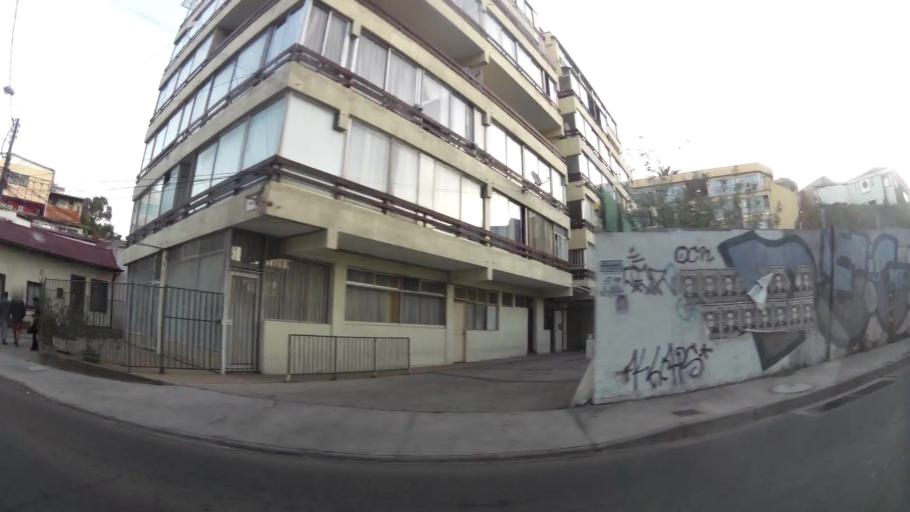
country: CL
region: Valparaiso
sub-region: Provincia de Valparaiso
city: Vina del Mar
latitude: -33.0245
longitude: -71.5665
